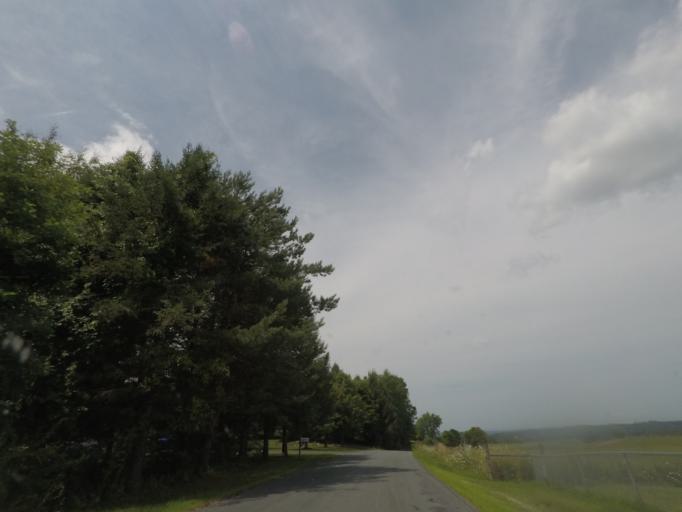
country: US
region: New York
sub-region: Rensselaer County
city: Wynantskill
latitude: 42.7128
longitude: -73.6411
